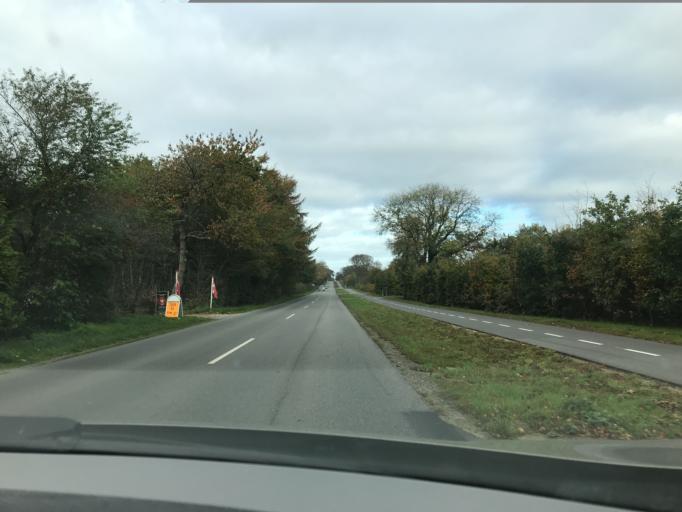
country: DK
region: South Denmark
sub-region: Kolding Kommune
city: Kolding
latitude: 55.5483
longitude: 9.4133
